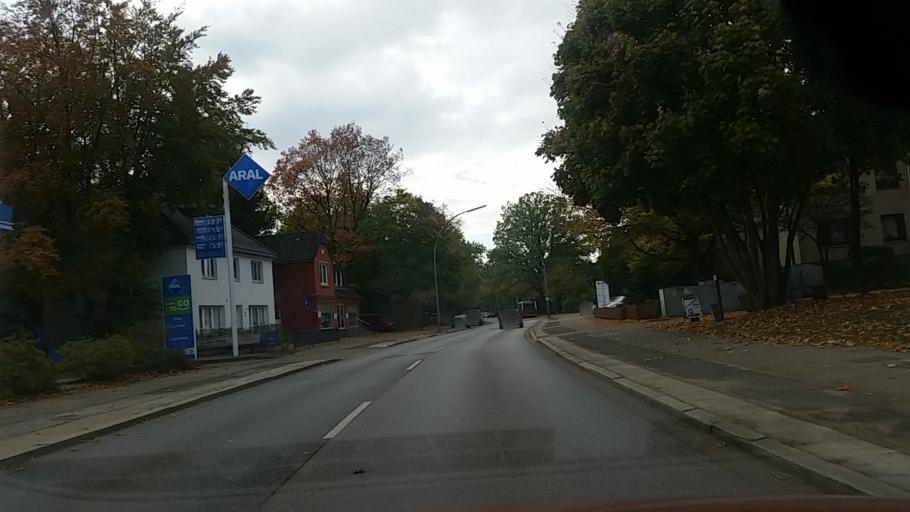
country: DE
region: Hamburg
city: Ohlsdorf
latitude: 53.6374
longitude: 10.0346
